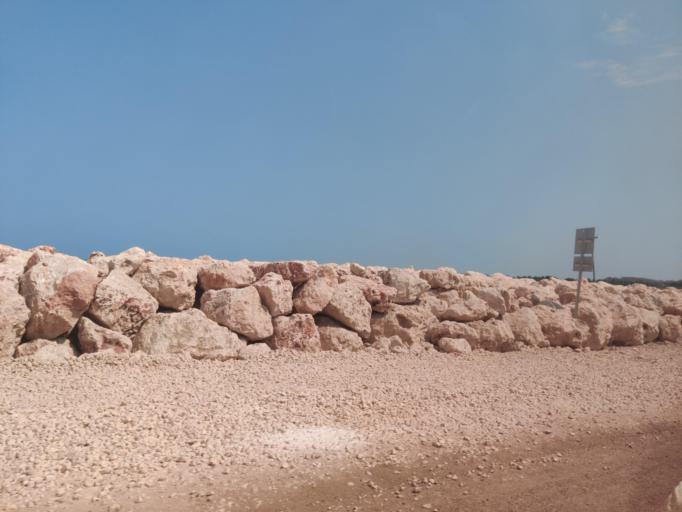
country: CO
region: Bolivar
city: Turbana
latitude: 10.1897
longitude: -75.6350
